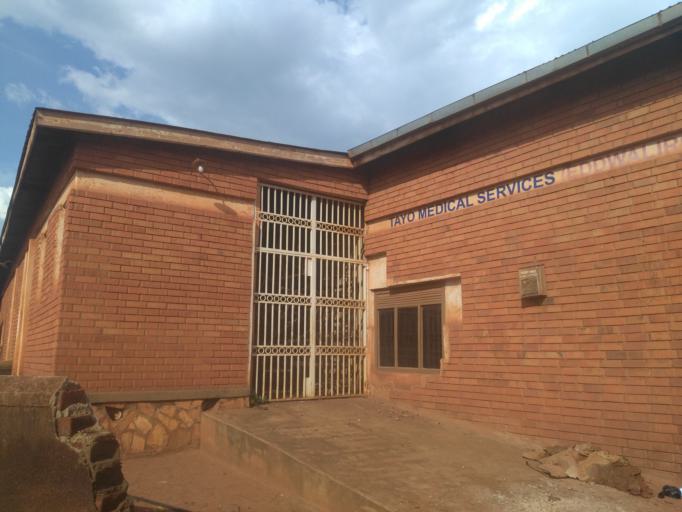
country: UG
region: Central Region
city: Kampala Central Division
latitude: 0.3616
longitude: 32.5735
